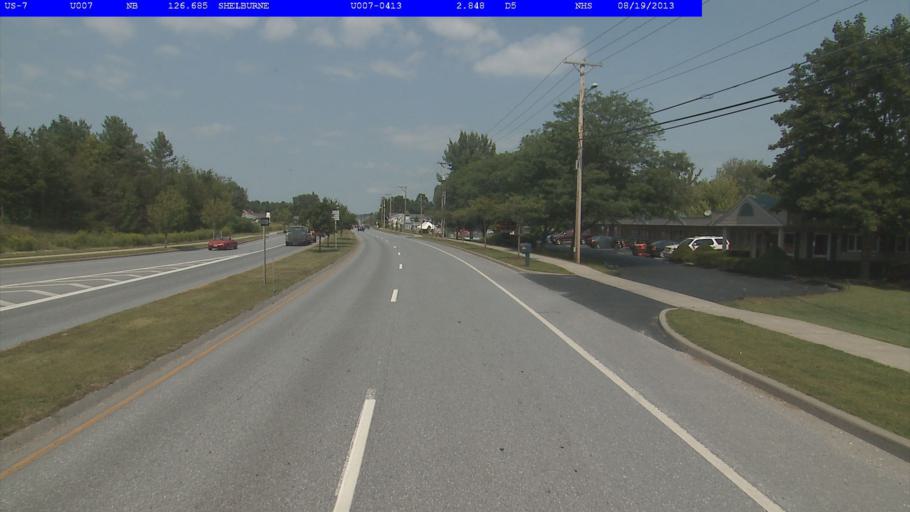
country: US
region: Vermont
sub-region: Chittenden County
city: Burlington
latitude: 44.3916
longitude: -73.2213
